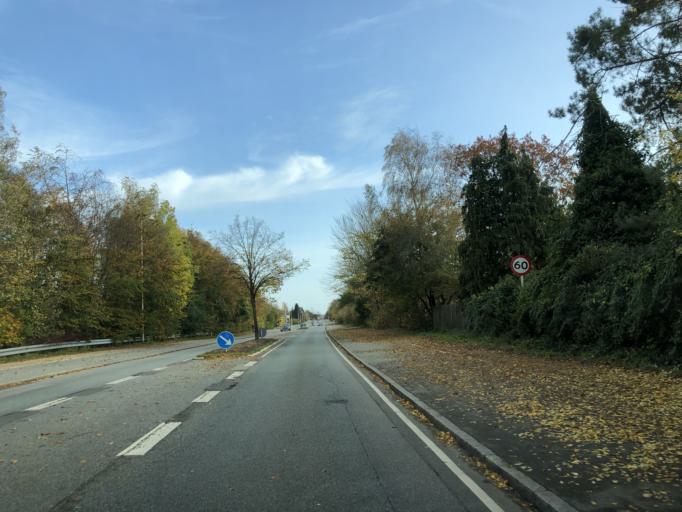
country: DK
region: Capital Region
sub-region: Rudersdal Kommune
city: Birkerod
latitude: 55.8508
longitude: 12.4217
